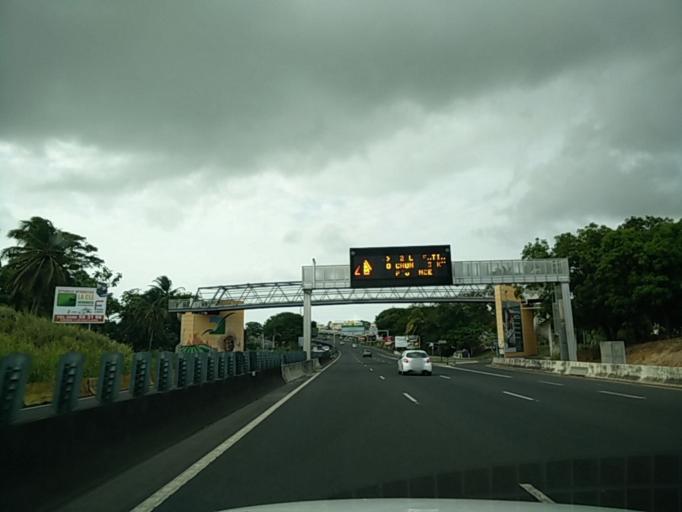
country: GP
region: Guadeloupe
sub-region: Guadeloupe
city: Baie-Mahault
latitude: 16.2339
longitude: -61.5900
